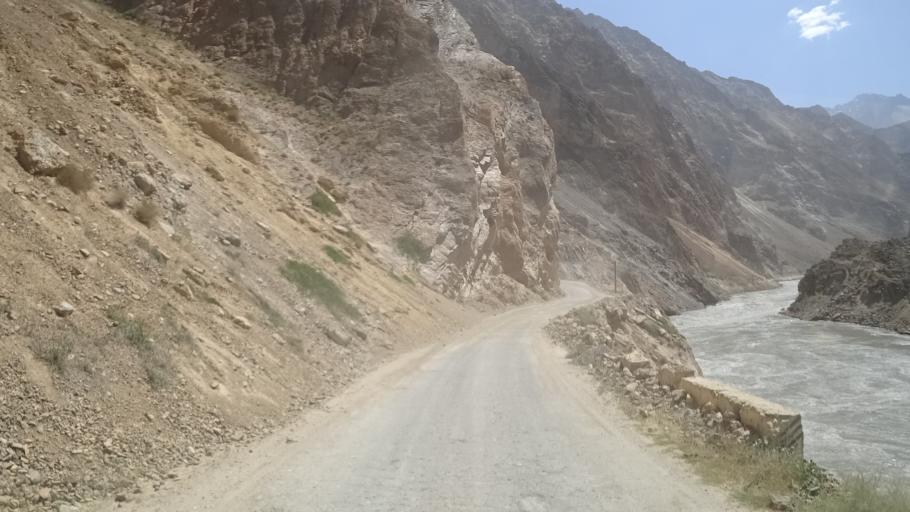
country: TJ
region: Gorno-Badakhshan
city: Vanj
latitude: 38.2717
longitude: 71.3528
